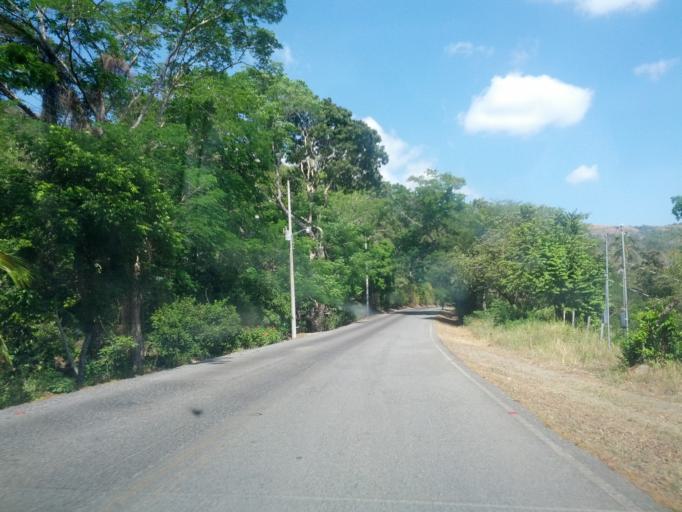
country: CR
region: Puntarenas
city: Buenos Aires
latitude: 8.9663
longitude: -83.3076
